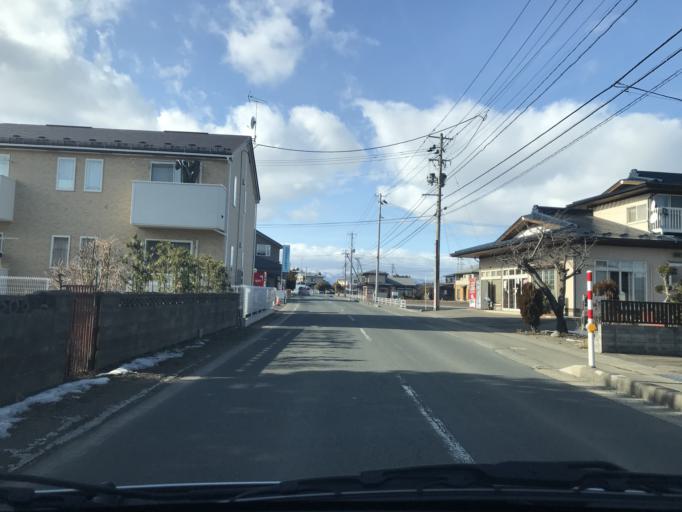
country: JP
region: Iwate
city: Kitakami
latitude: 39.3032
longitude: 141.1002
